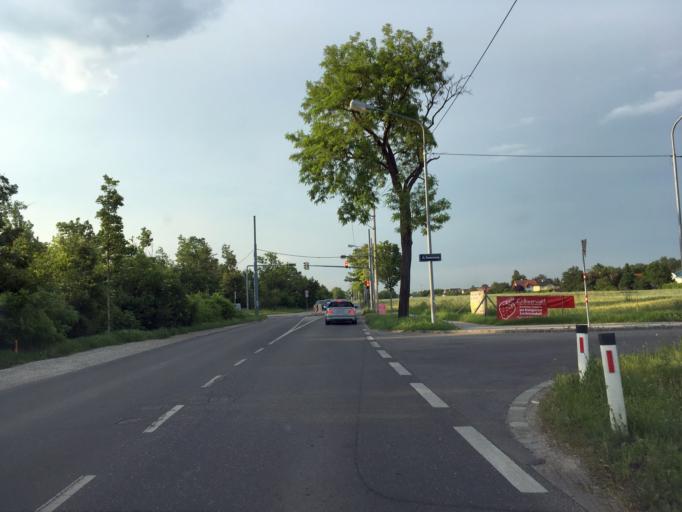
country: AT
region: Lower Austria
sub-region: Politischer Bezirk Wien-Umgebung
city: Gerasdorf bei Wien
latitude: 48.2740
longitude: 16.4574
